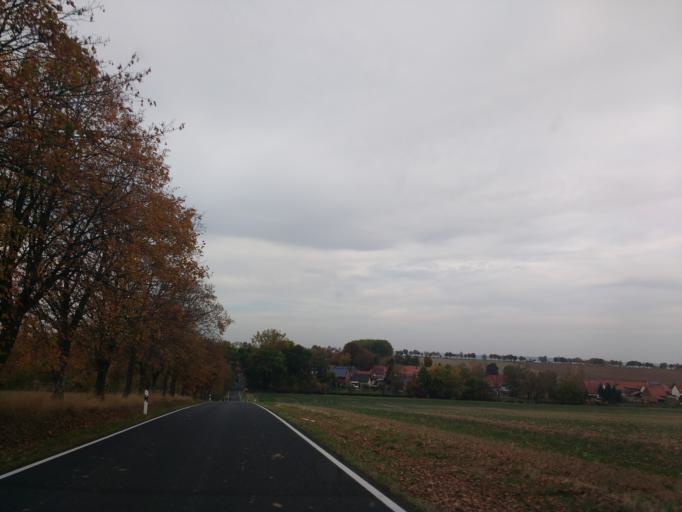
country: DE
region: Thuringia
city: Heroldishausen
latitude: 51.1334
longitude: 10.5160
